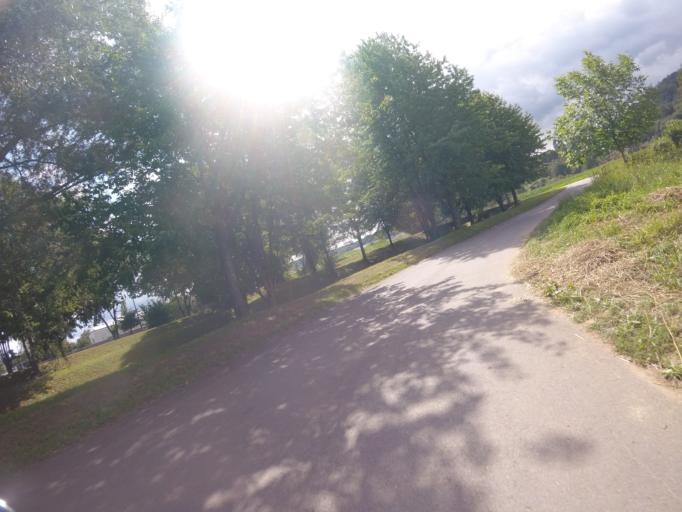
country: DE
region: Baden-Wuerttemberg
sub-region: Regierungsbezirk Stuttgart
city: Winterbach
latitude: 48.8031
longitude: 9.4685
